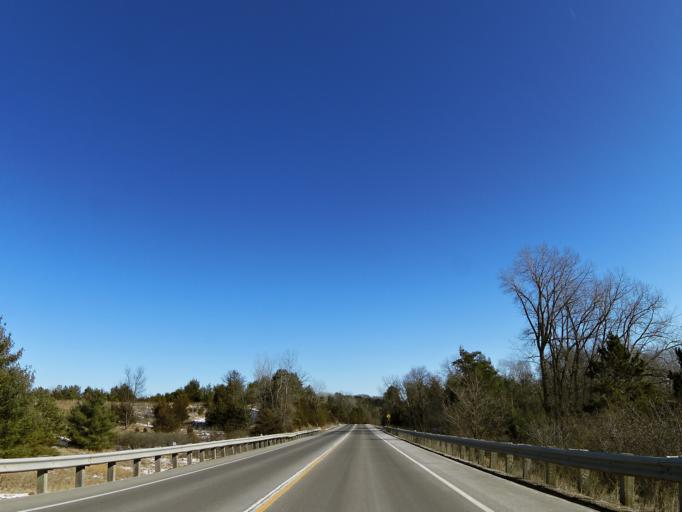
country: US
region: Minnesota
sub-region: Washington County
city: Stillwater
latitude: 45.0767
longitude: -92.8208
